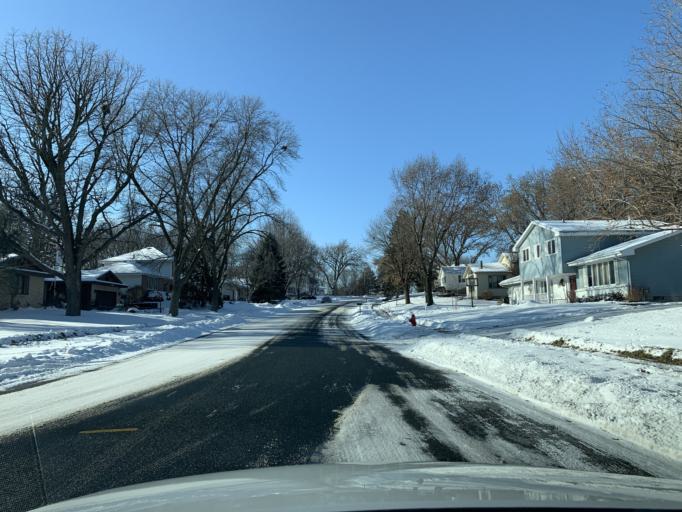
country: US
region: Minnesota
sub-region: Scott County
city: Savage
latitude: 44.8202
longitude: -93.3414
